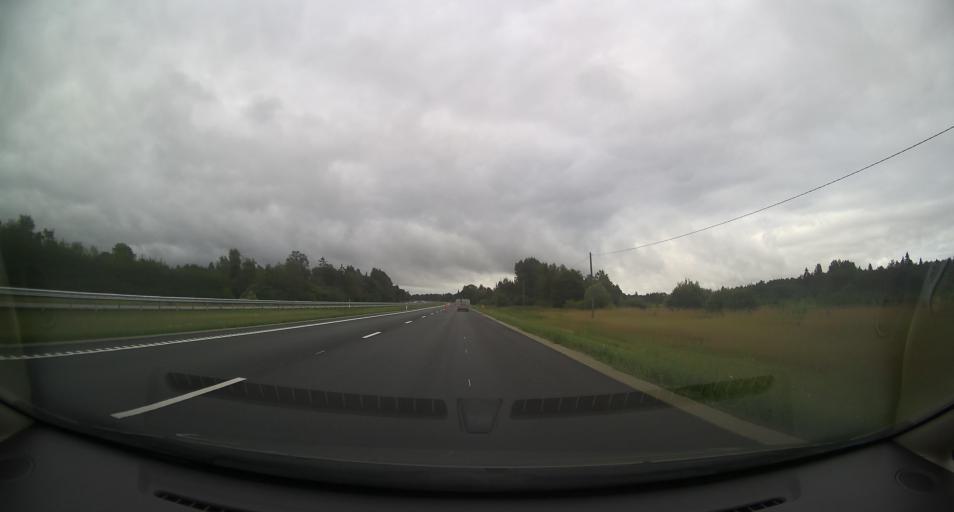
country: EE
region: Harju
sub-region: Rae vald
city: Vaida
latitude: 59.3069
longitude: 24.9466
